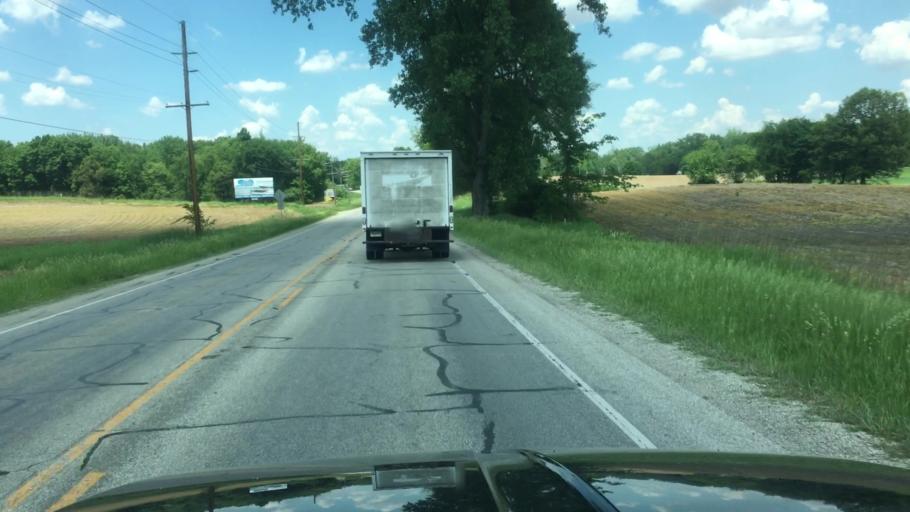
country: US
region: Indiana
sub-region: Kosciusko County
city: North Webster
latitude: 41.3109
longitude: -85.6910
